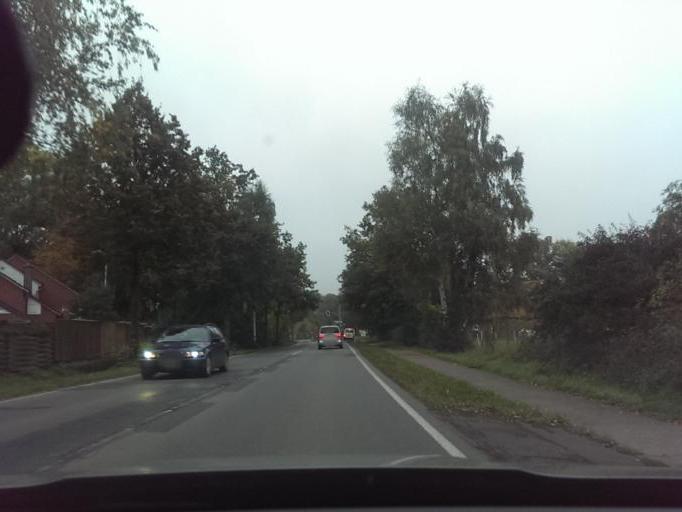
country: DE
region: Lower Saxony
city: Garbsen-Mitte
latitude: 52.5042
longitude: 9.6305
